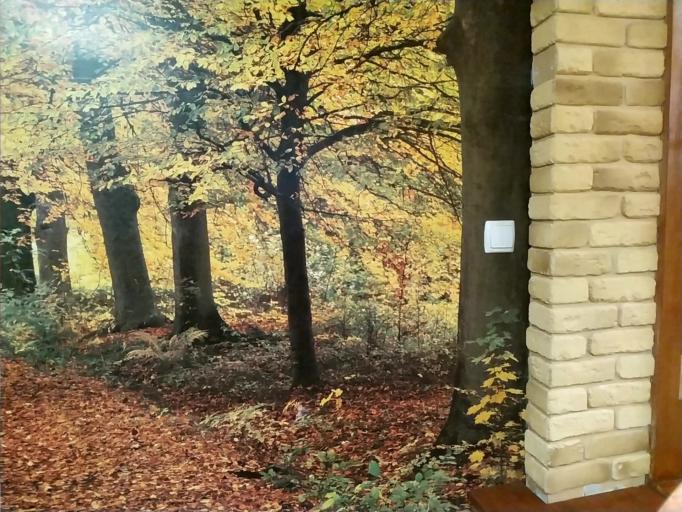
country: RU
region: Smolensk
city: Safonovo
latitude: 55.1975
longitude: 33.1748
